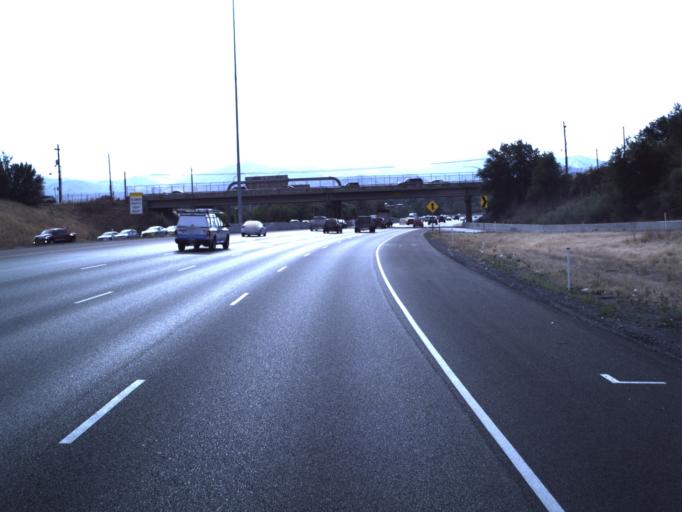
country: US
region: Utah
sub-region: Salt Lake County
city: Midvale
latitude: 40.6362
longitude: -111.9082
